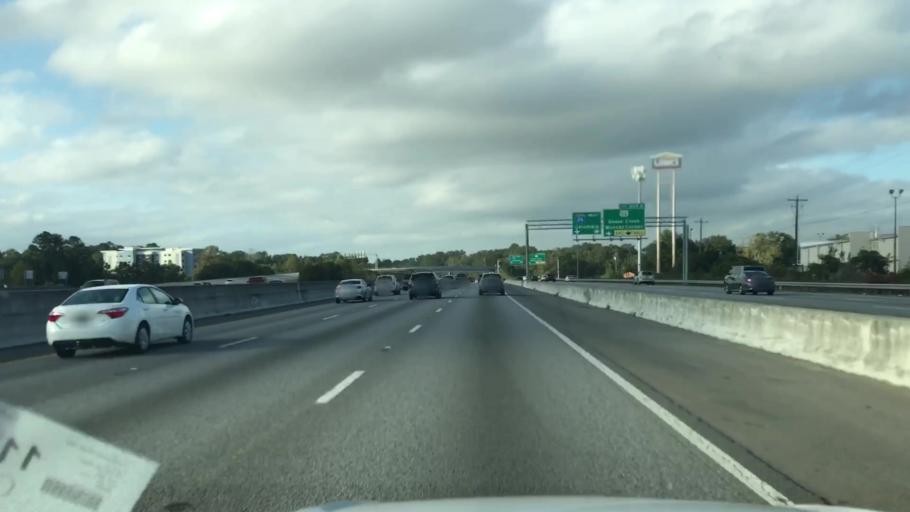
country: US
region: South Carolina
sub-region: Berkeley County
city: Hanahan
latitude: 32.9365
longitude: -80.0483
